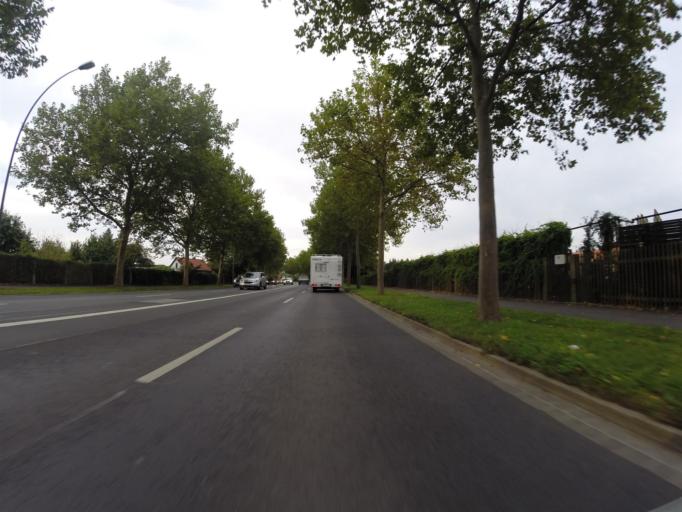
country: DE
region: Saxony
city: Albertstadt
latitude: 51.0816
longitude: 13.7395
